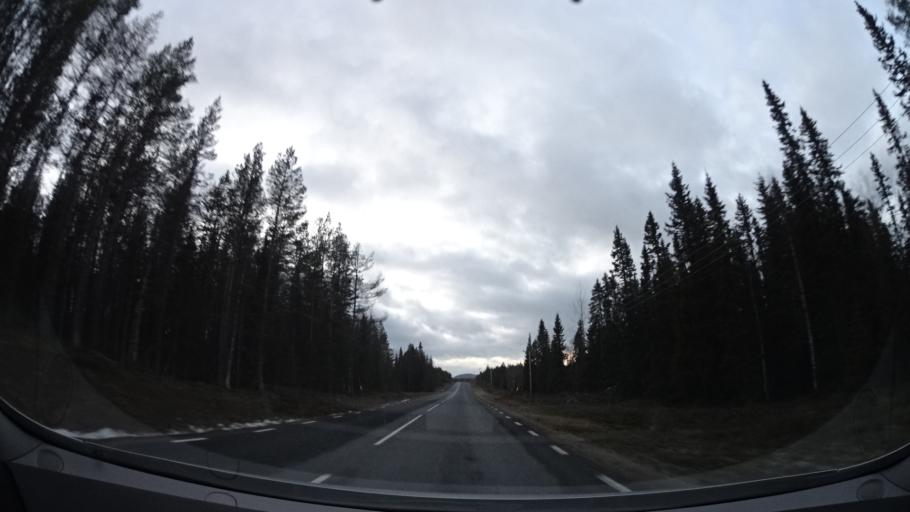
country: SE
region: Vaesterbotten
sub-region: Asele Kommun
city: Insjon
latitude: 64.3635
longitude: 17.9455
